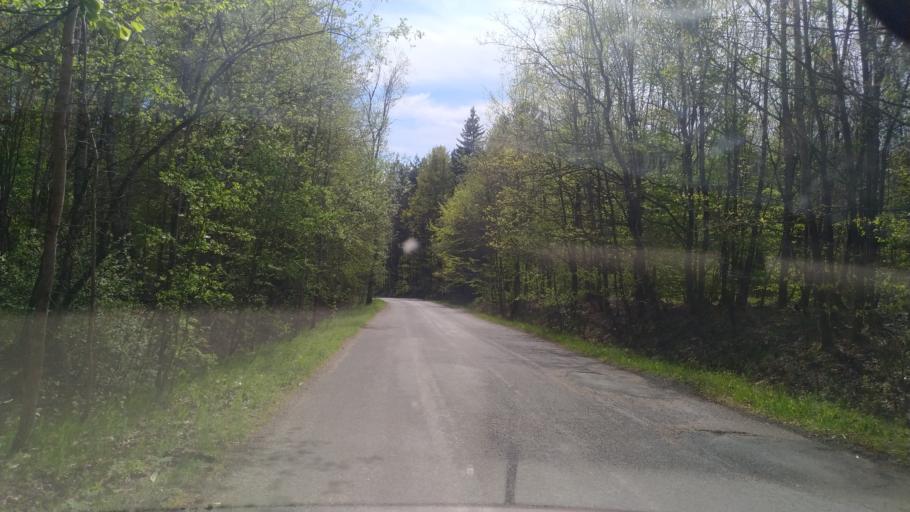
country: PL
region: West Pomeranian Voivodeship
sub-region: Powiat walecki
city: Miroslawiec
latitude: 53.3543
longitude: 16.2771
